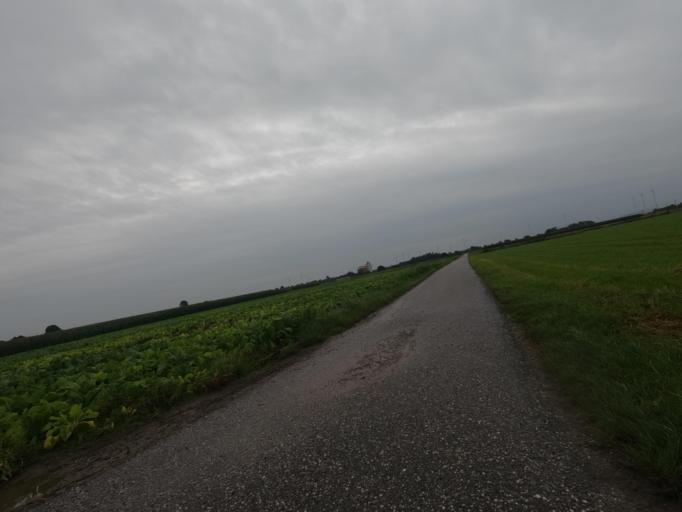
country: DE
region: North Rhine-Westphalia
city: Huckelhoven
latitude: 51.0008
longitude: 6.1963
